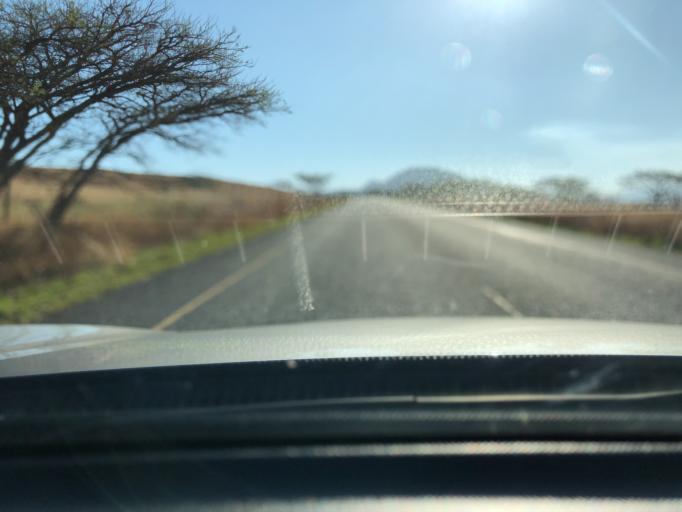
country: ZA
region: KwaZulu-Natal
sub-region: uThukela District Municipality
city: Ladysmith
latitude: -28.4023
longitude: 29.9399
